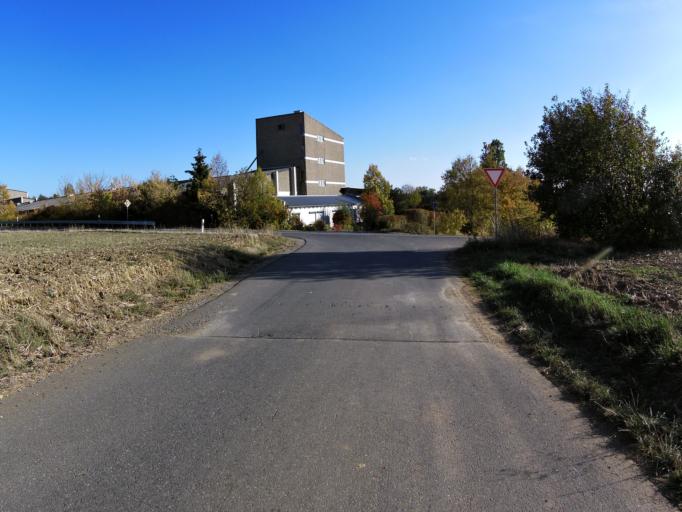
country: DE
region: Bavaria
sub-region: Regierungsbezirk Unterfranken
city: Reichenberg
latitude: 49.7144
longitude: 9.9370
